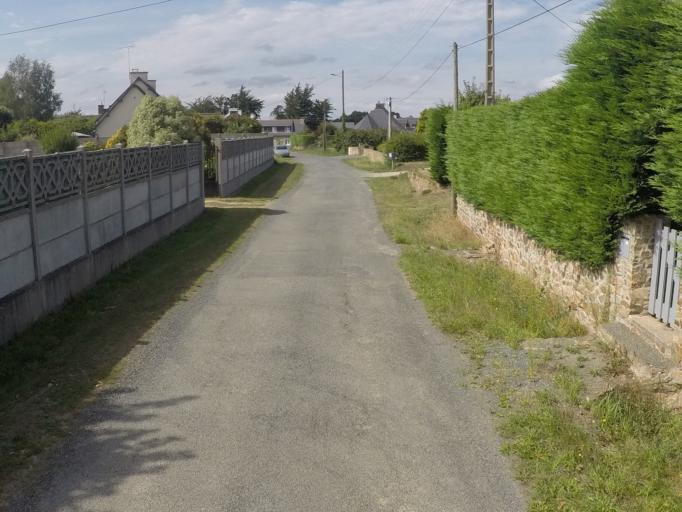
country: FR
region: Brittany
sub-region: Departement des Cotes-d'Armor
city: Goudelin
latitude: 48.6059
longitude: -3.0130
